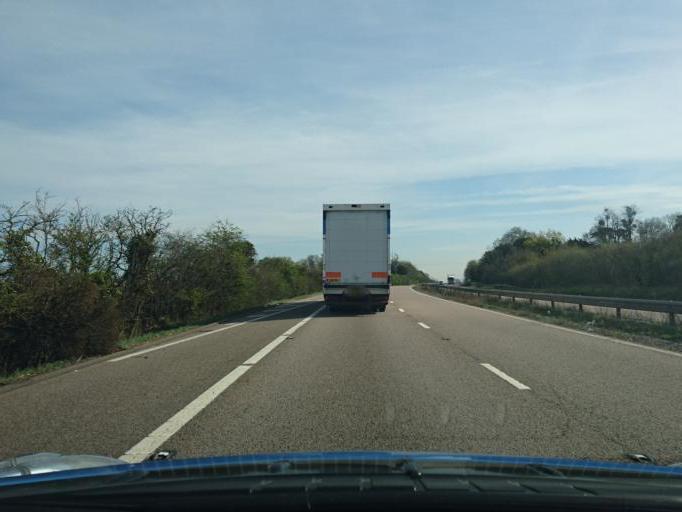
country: GB
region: England
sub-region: Worcestershire
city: Upton upon Severn
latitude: 52.0154
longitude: -2.2330
